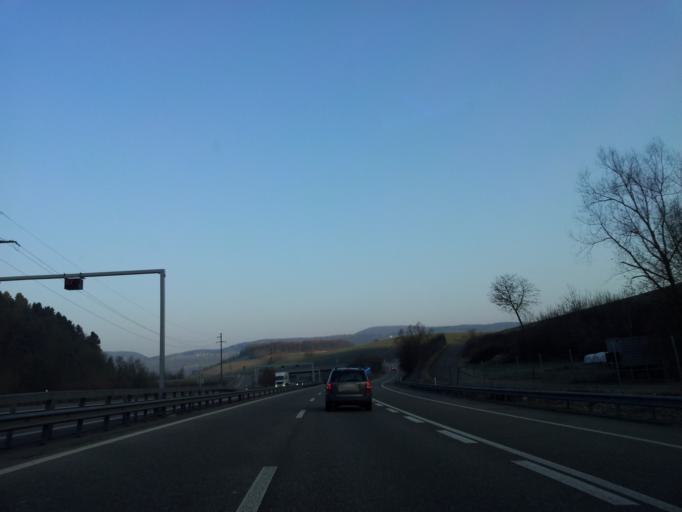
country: CH
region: Aargau
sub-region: Bezirk Aarau
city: Densbueren
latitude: 47.4811
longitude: 8.0973
